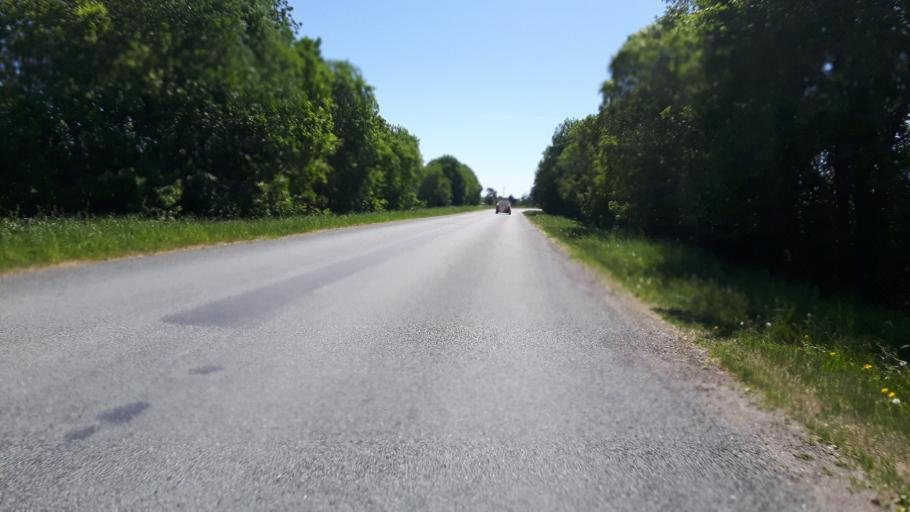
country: EE
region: Harju
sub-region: Kuusalu vald
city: Kuusalu
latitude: 59.5092
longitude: 25.5202
